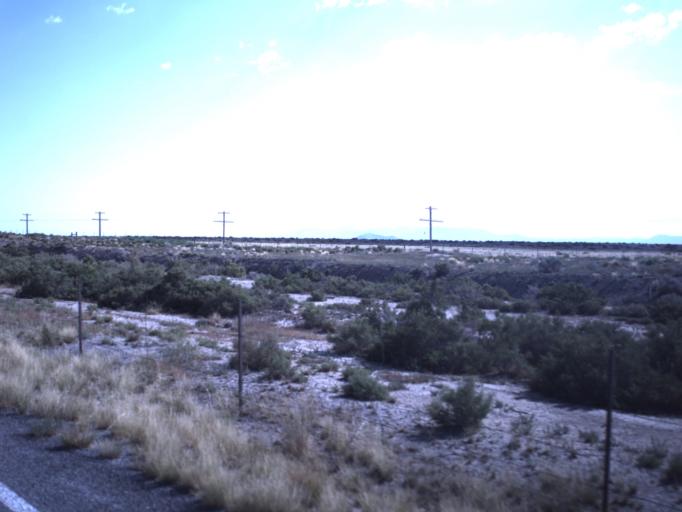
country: US
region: Utah
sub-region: Millard County
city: Delta
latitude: 38.9537
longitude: -112.8054
